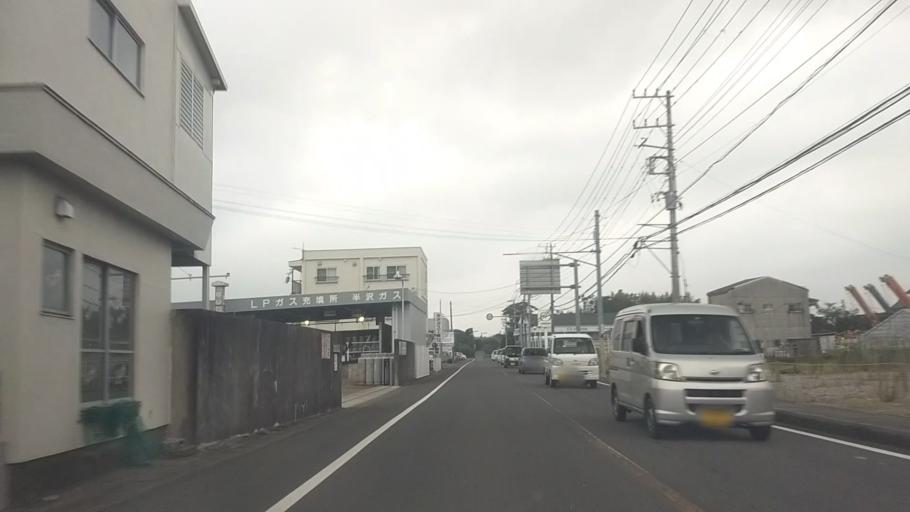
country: JP
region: Chiba
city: Kawaguchi
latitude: 35.1067
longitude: 140.0943
